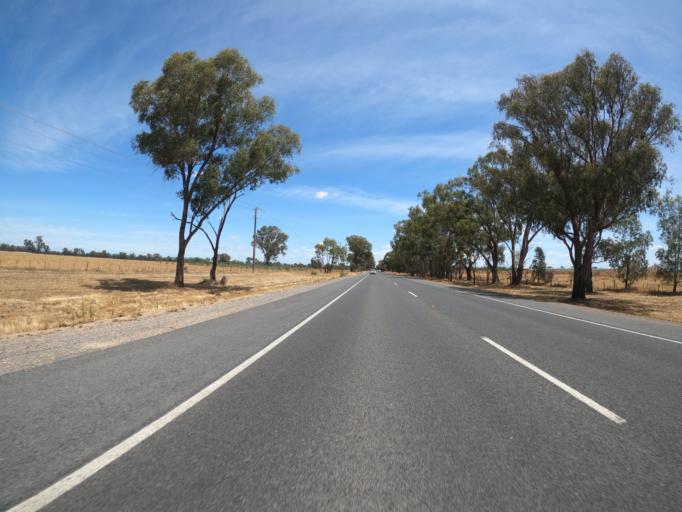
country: AU
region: Victoria
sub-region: Benalla
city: Benalla
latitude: -36.5266
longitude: 146.0495
